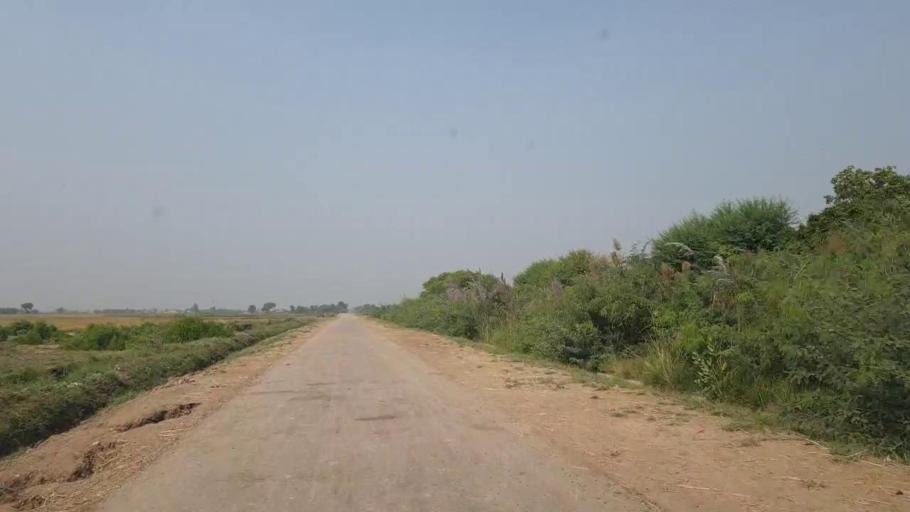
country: PK
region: Sindh
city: Matli
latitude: 25.1449
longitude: 68.7046
